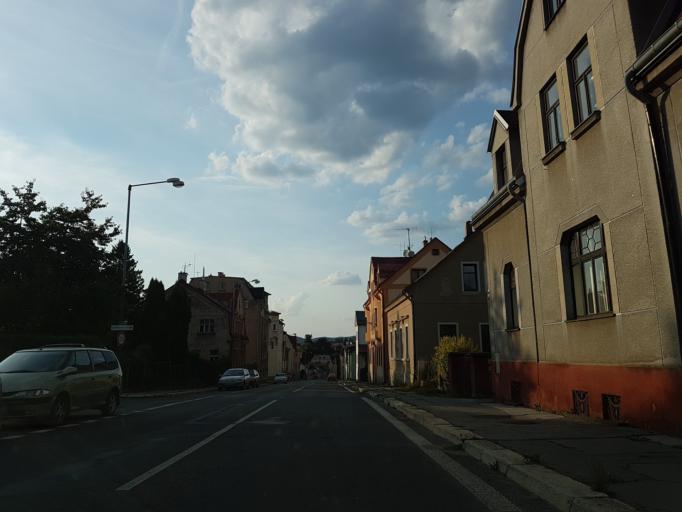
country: CZ
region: Liberecky
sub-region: Okres Jablonec nad Nisou
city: Jablonec nad Nisou
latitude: 50.7208
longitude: 15.1831
